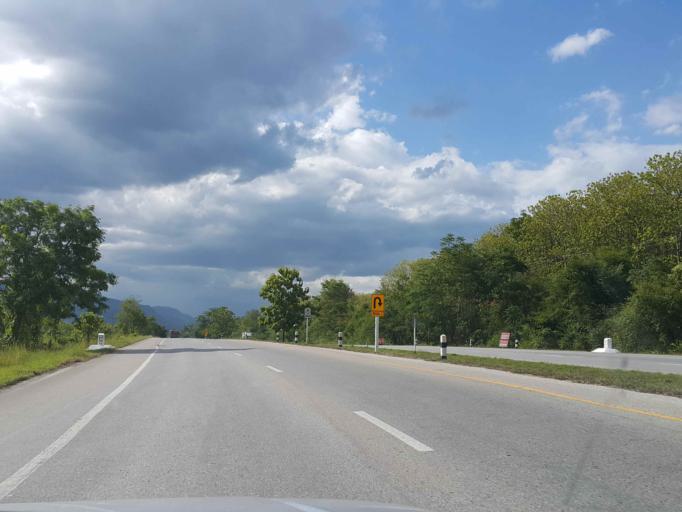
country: TH
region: Lampang
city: Thoen
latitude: 17.6974
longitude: 99.2331
